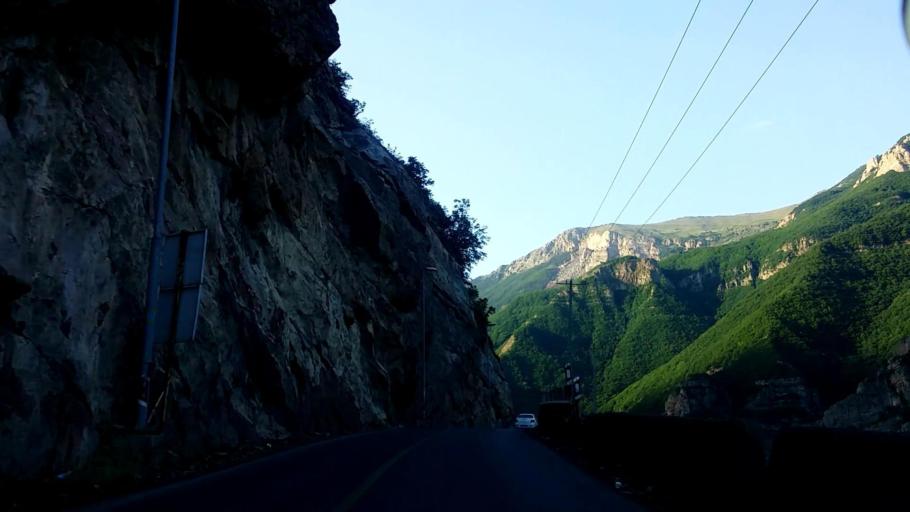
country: IR
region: Mazandaran
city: Chalus
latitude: 36.2583
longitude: 51.2754
